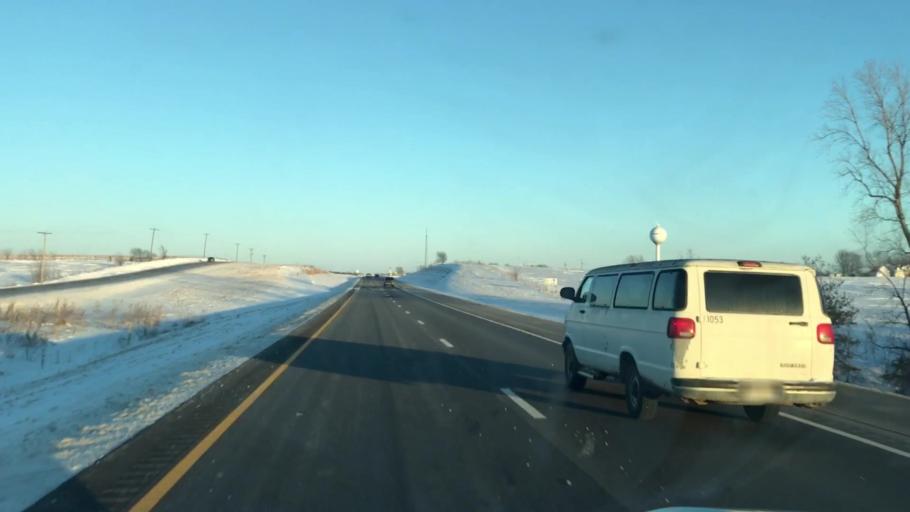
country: US
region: Missouri
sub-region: Clinton County
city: Gower
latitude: 39.7620
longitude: -94.5132
